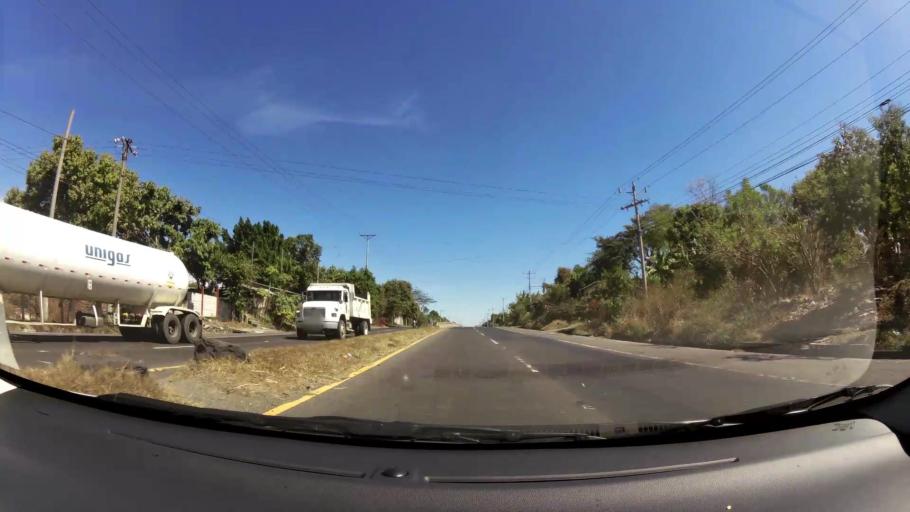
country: SV
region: La Libertad
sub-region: Distrito de Quezaltepeque
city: Quezaltepeque
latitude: 13.8114
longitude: -89.3187
